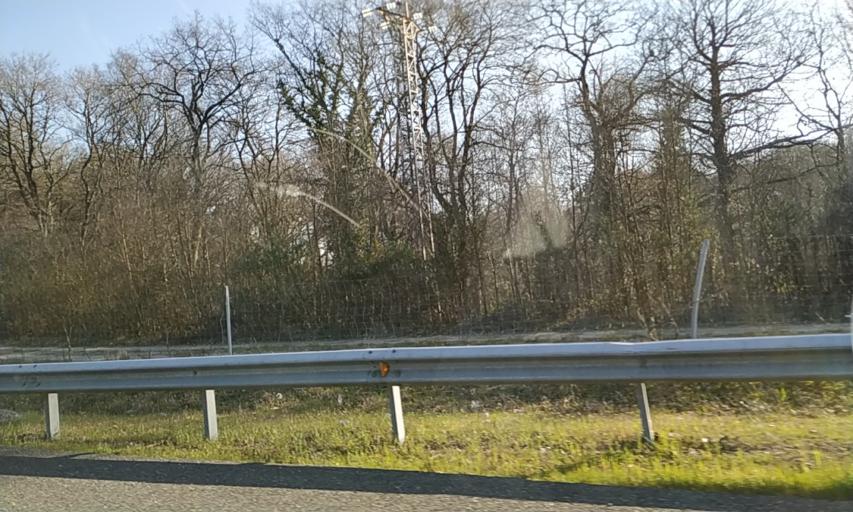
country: ES
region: Galicia
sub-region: Provincia de Lugo
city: Lugo
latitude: 43.0449
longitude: -7.5280
